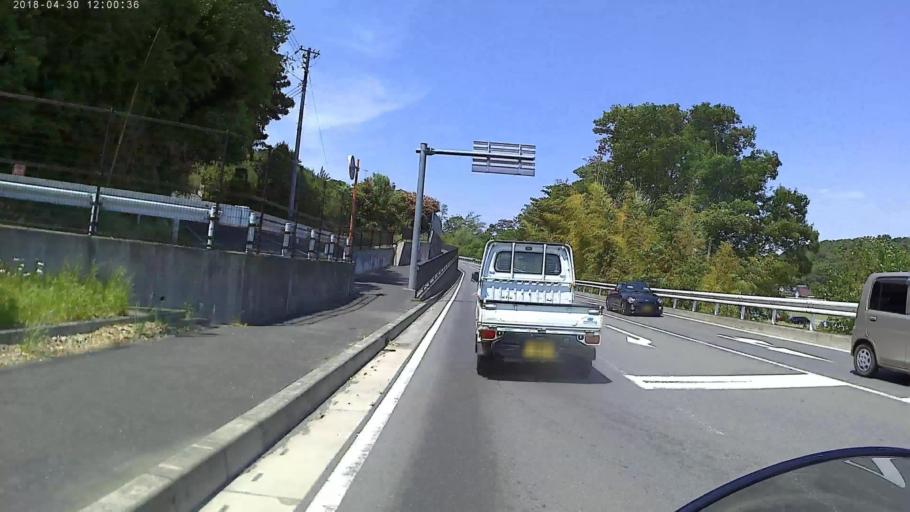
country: JP
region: Kanagawa
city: Zama
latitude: 35.5120
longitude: 139.3282
